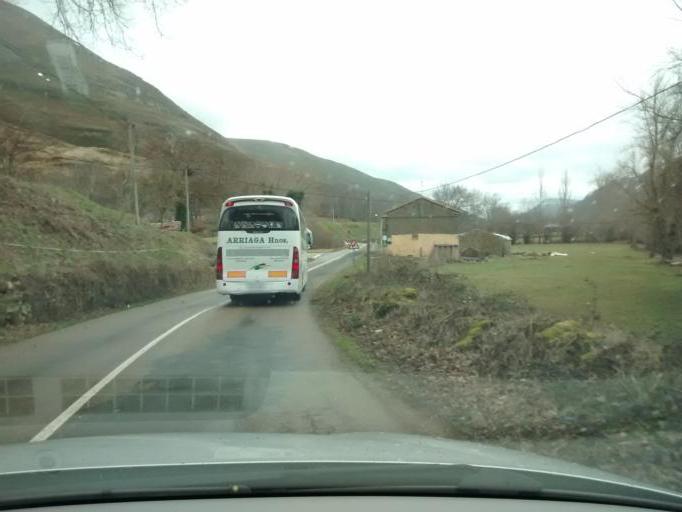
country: ES
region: Castille and Leon
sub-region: Provincia de Burgos
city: Espinosa de los Monteros
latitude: 43.1178
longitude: -3.5842
